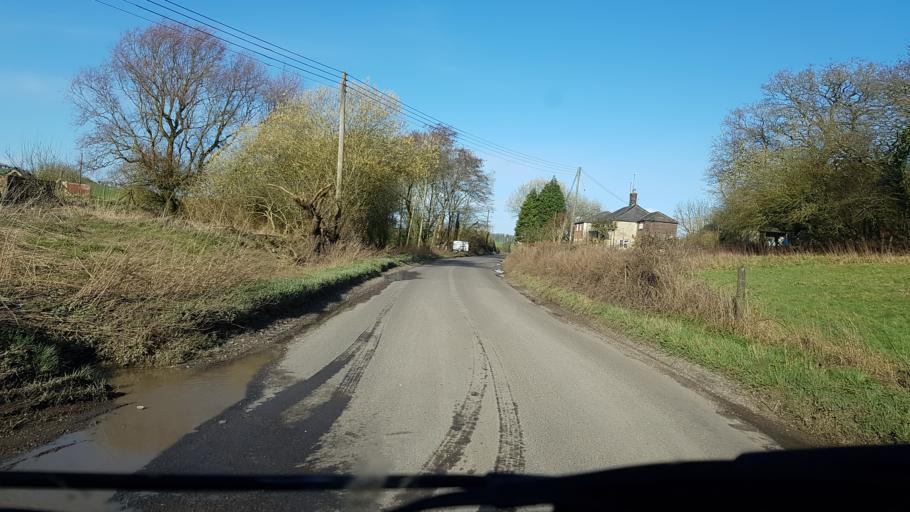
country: GB
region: England
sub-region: Wiltshire
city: Huish
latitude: 51.3930
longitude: -1.8162
